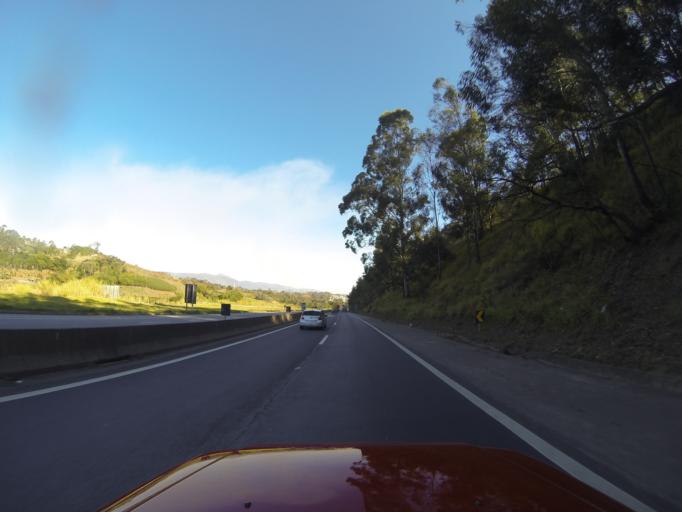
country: BR
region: Sao Paulo
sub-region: Atibaia
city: Atibaia
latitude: -23.0794
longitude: -46.5699
